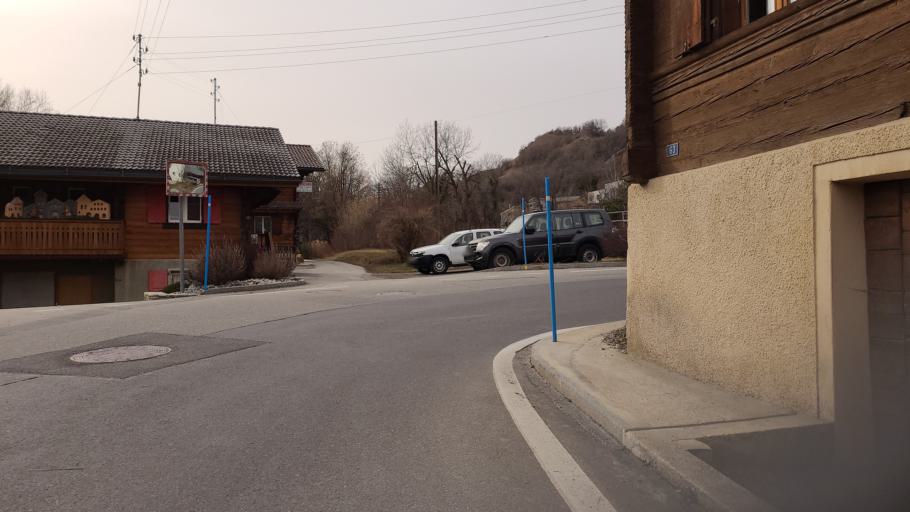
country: CH
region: Valais
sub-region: Sion District
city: Grimisuat
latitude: 46.2629
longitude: 7.3990
